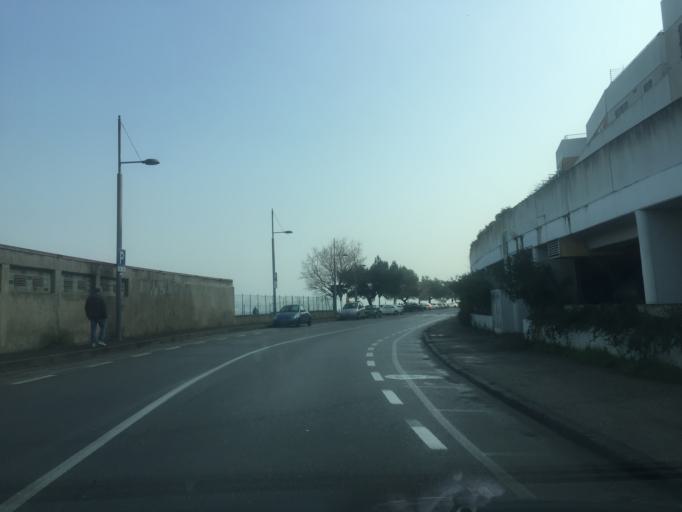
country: IT
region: Friuli Venezia Giulia
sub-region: Provincia di Trieste
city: Muggia
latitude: 45.6069
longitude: 13.7594
